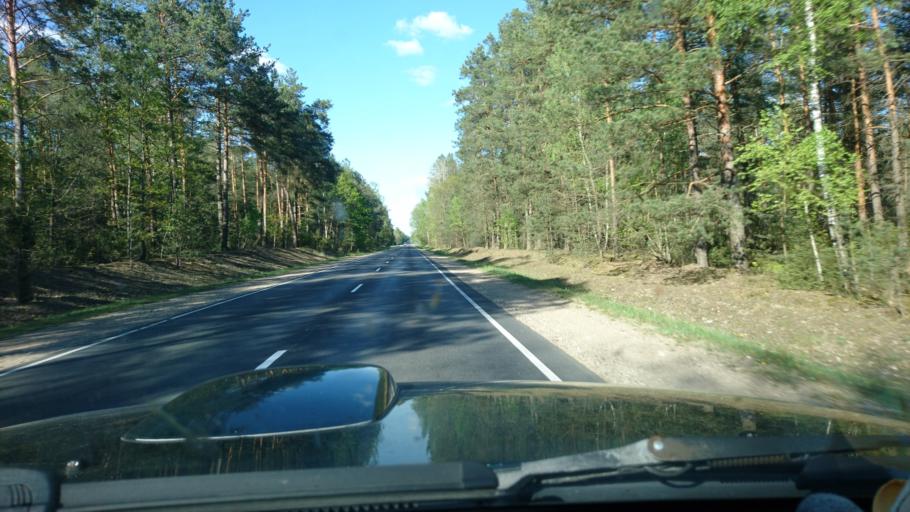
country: BY
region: Brest
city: Pruzhany
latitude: 52.4551
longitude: 24.3001
